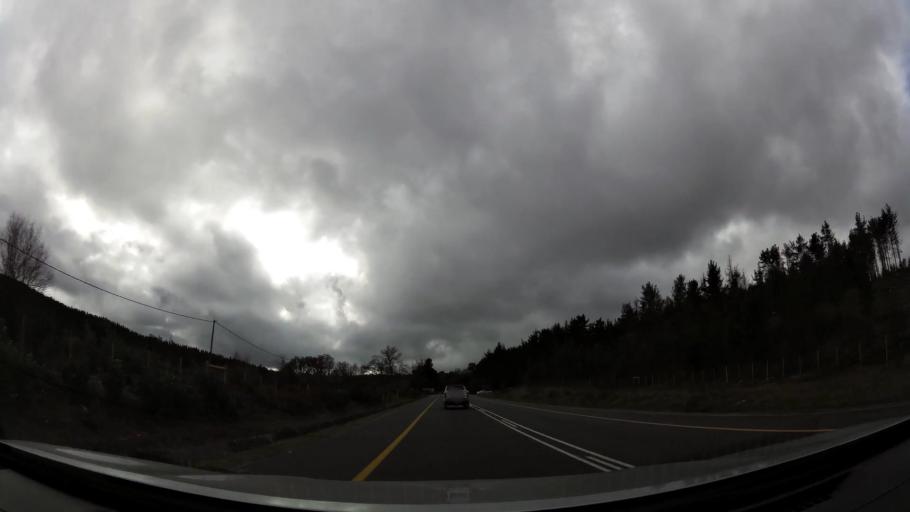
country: ZA
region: Western Cape
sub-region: Eden District Municipality
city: Knysna
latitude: -34.0307
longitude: 23.1589
